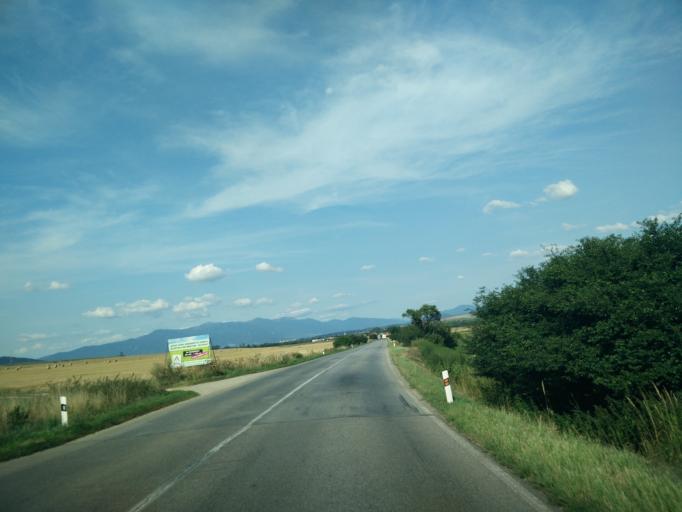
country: SK
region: Zilinsky
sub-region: Okres Martin
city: Martin
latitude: 48.9809
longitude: 18.8537
